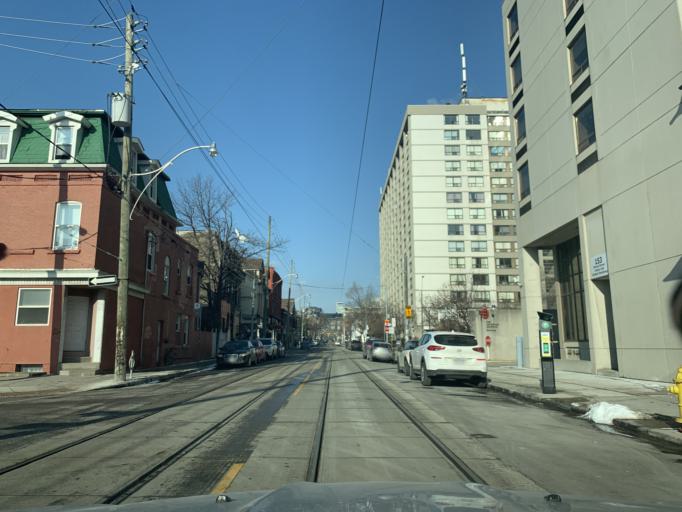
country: CA
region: Ontario
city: Toronto
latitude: 43.6552
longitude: -79.3918
